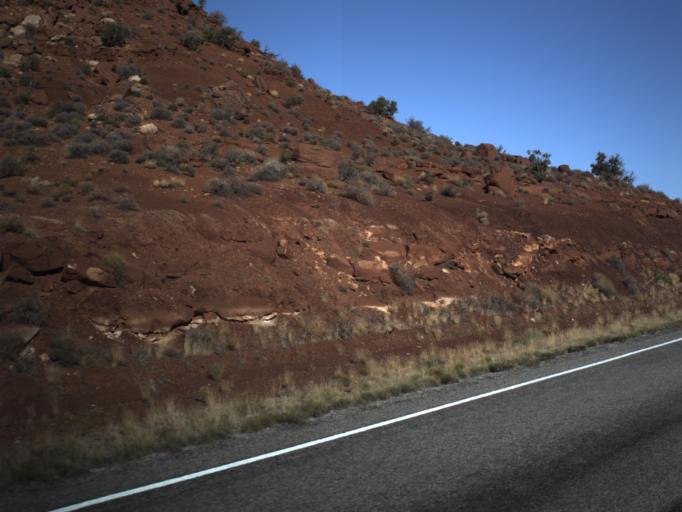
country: US
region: Utah
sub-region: San Juan County
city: Blanding
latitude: 37.7097
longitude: -110.2422
